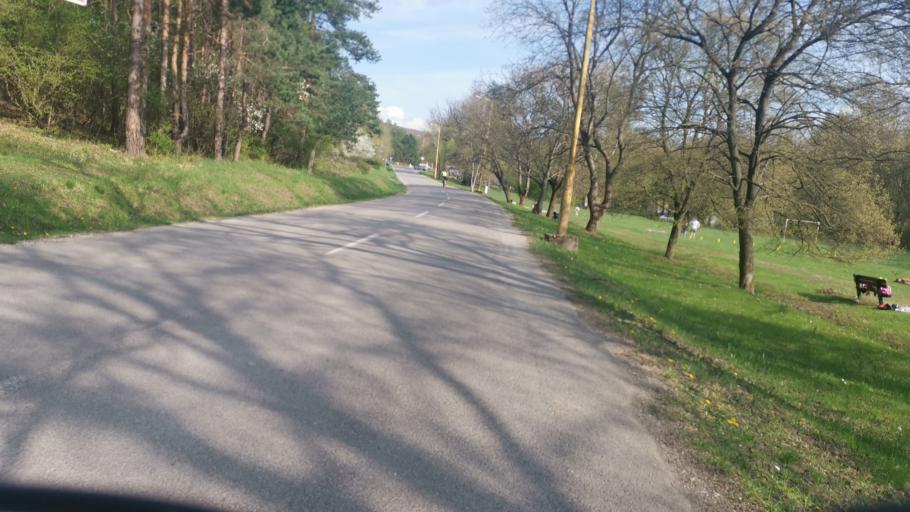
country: CZ
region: South Moravian
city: Sudomerice
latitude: 48.8270
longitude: 17.2963
